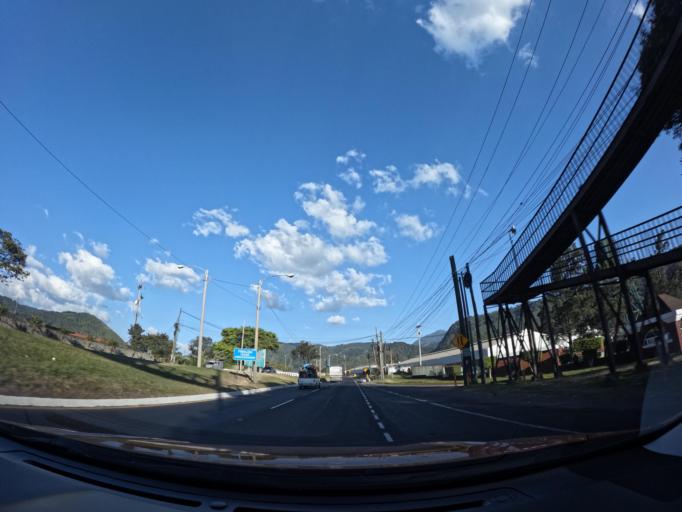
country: GT
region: Escuintla
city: Palin
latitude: 14.4107
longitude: -90.6807
